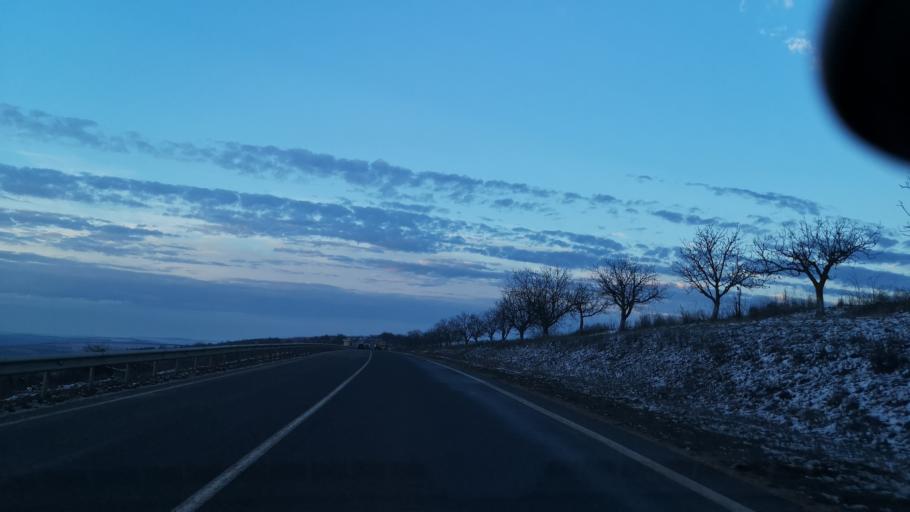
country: MD
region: Rezina
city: Saharna
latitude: 47.6020
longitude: 28.8321
